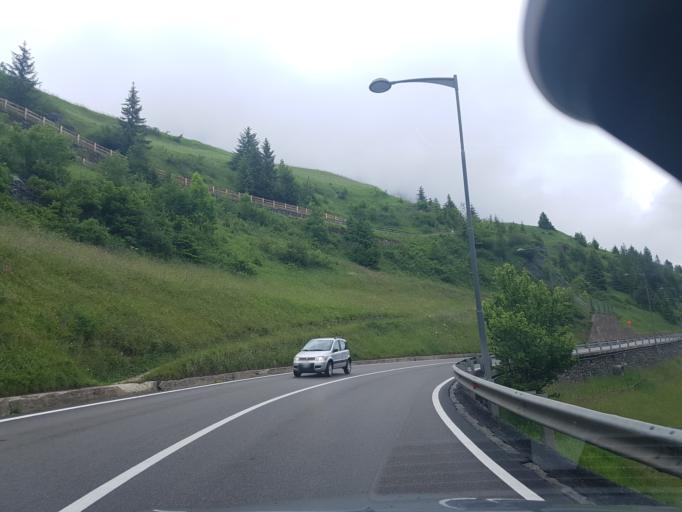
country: IT
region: Trentino-Alto Adige
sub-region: Bolzano
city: Santa Cristina Valgardena
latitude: 46.5594
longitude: 11.7346
